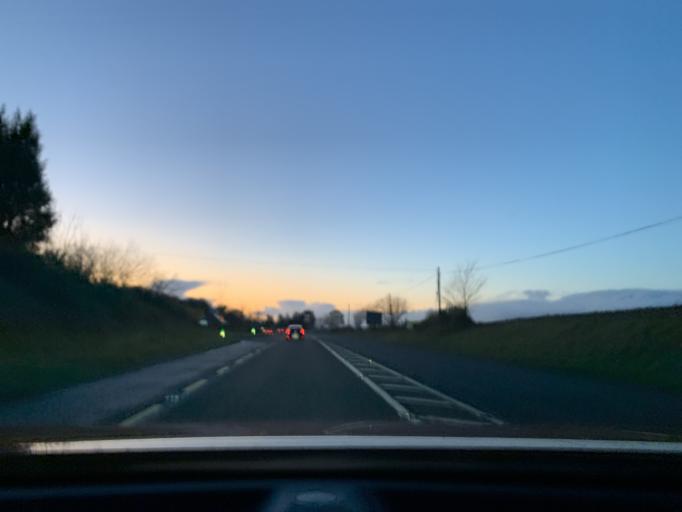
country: IE
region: Connaught
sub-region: Roscommon
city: Boyle
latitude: 53.9699
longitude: -8.2486
